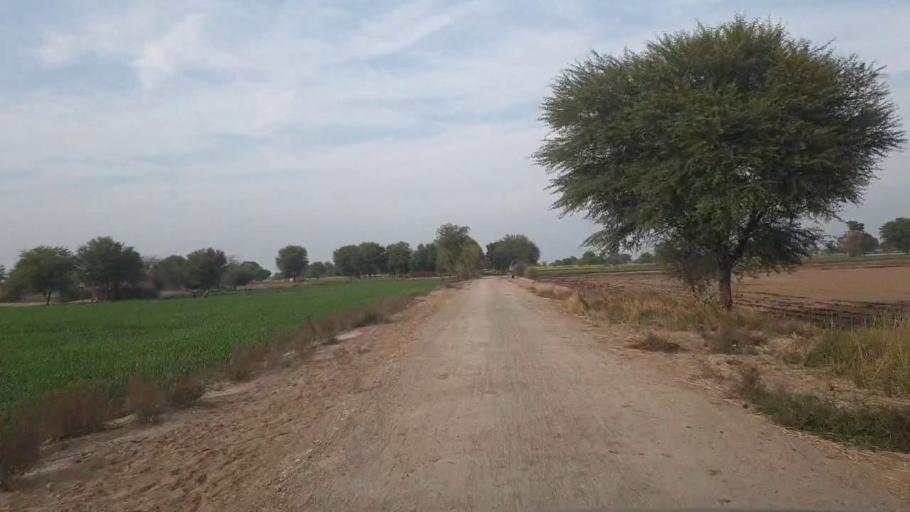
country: PK
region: Sindh
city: Shahpur Chakar
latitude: 26.1241
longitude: 68.5547
